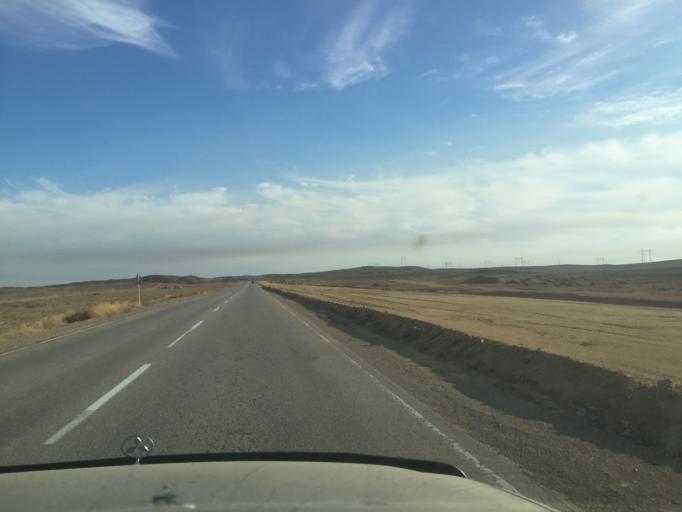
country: KZ
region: Zhambyl
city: Mynaral
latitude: 45.5212
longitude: 73.4881
